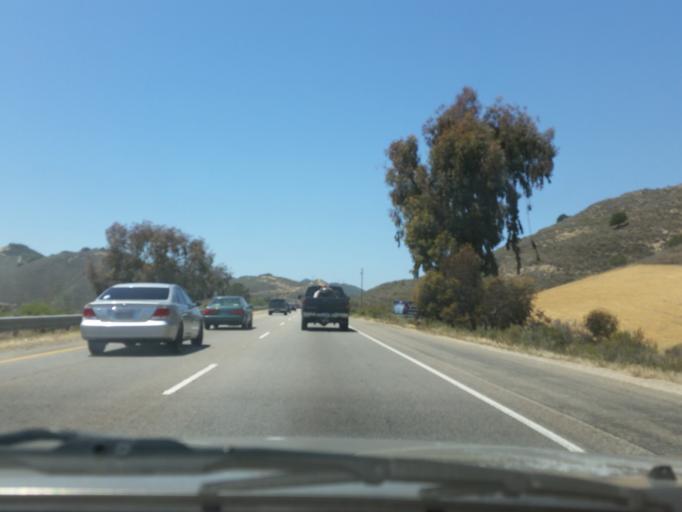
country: US
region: California
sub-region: San Luis Obispo County
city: Avila Beach
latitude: 35.1705
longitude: -120.6926
